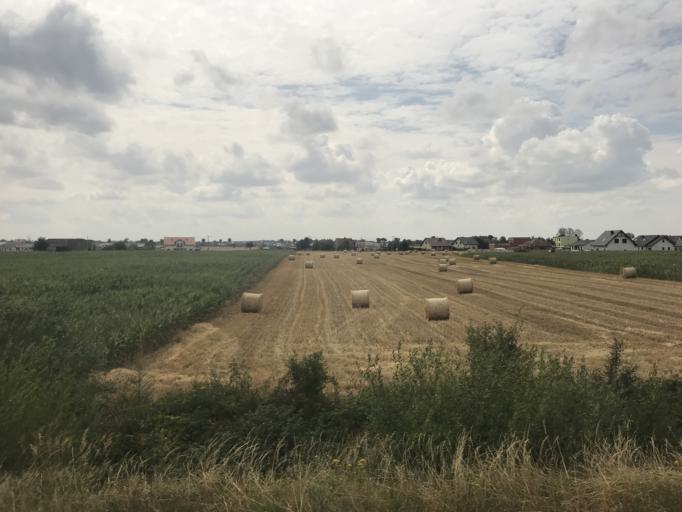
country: PL
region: Greater Poland Voivodeship
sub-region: Powiat gnieznienski
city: Gniezno
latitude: 52.5204
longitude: 17.5555
